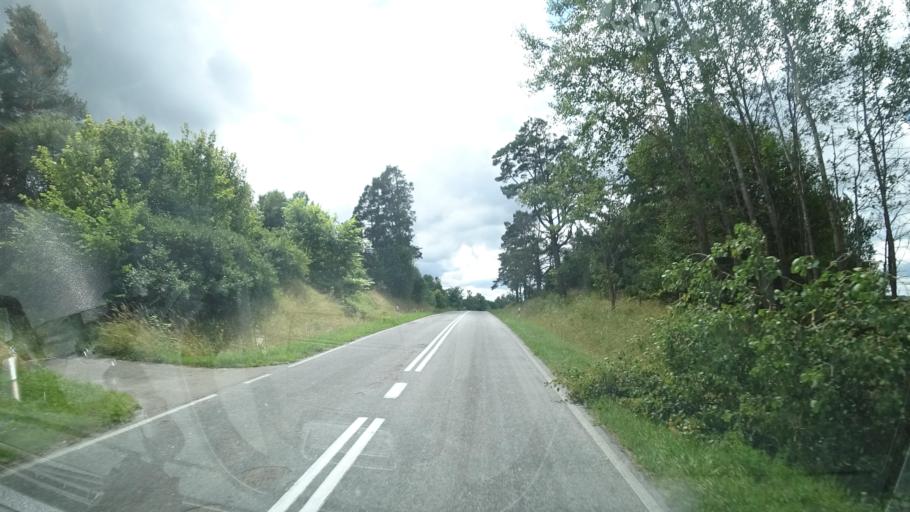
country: PL
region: Warmian-Masurian Voivodeship
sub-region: Powiat goldapski
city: Goldap
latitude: 54.2098
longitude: 22.2027
